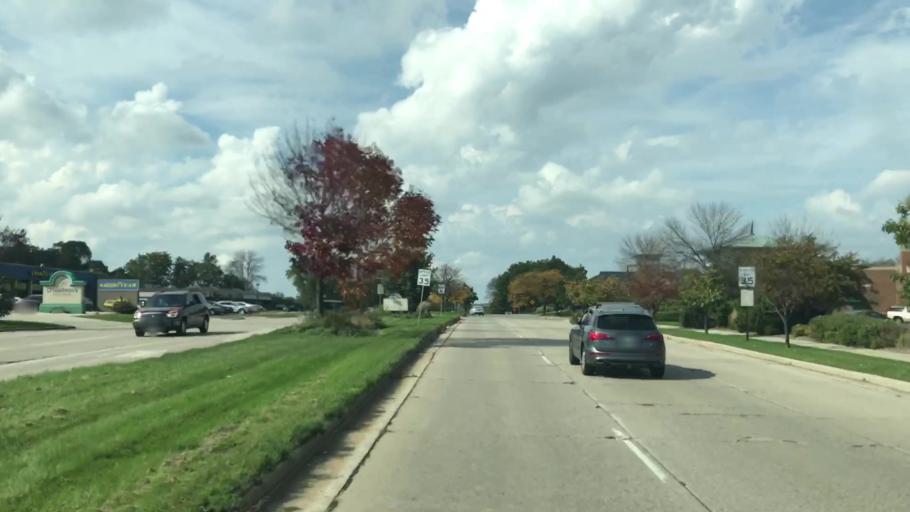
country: US
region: Wisconsin
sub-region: Waukesha County
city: Elm Grove
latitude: 43.0600
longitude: -88.0673
